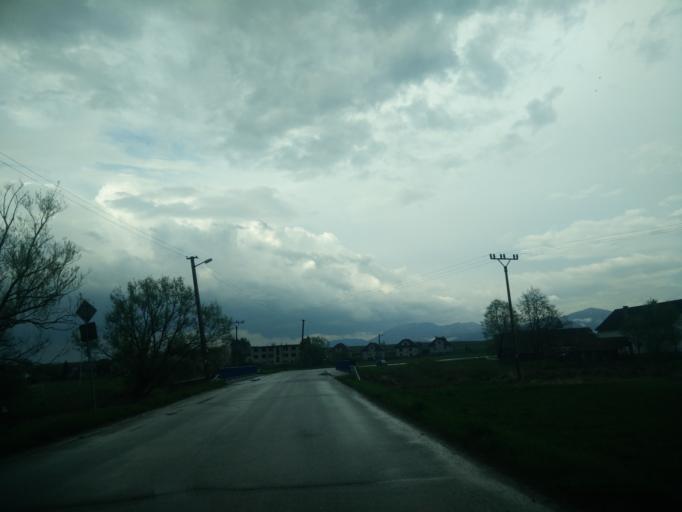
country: SK
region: Nitriansky
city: Handlova
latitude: 48.8639
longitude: 18.7989
